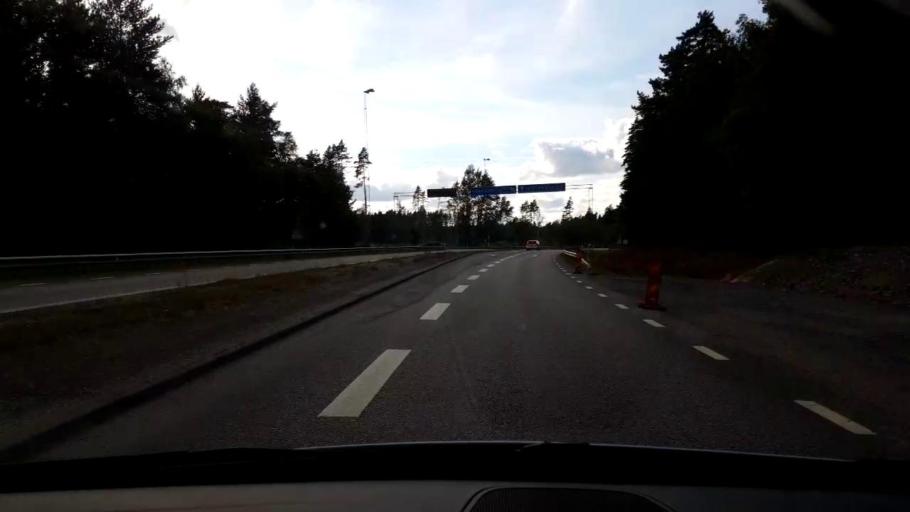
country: SE
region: Joenkoeping
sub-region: Savsjo Kommun
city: Vrigstad
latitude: 57.3661
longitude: 14.4346
